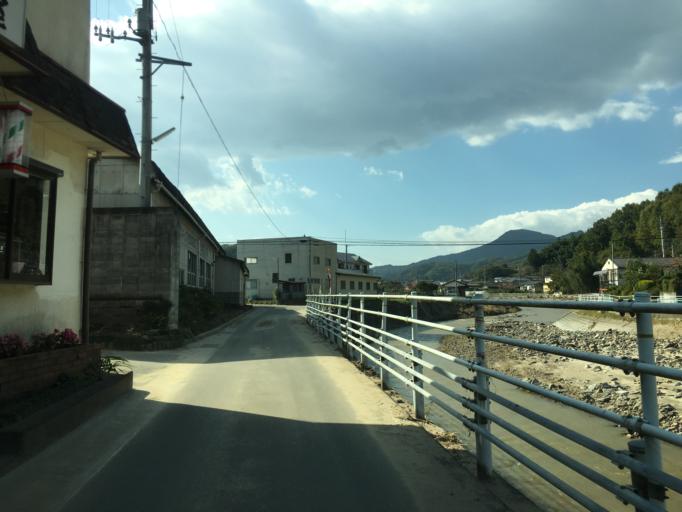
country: JP
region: Fukushima
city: Hobaramachi
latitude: 37.7336
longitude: 140.6072
